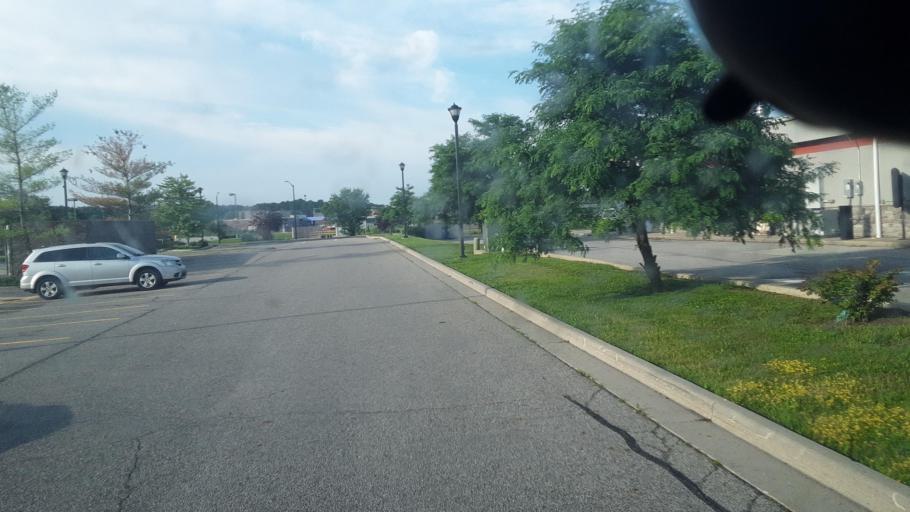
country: US
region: Indiana
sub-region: DeKalb County
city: Auburn
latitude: 41.3664
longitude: -85.0844
